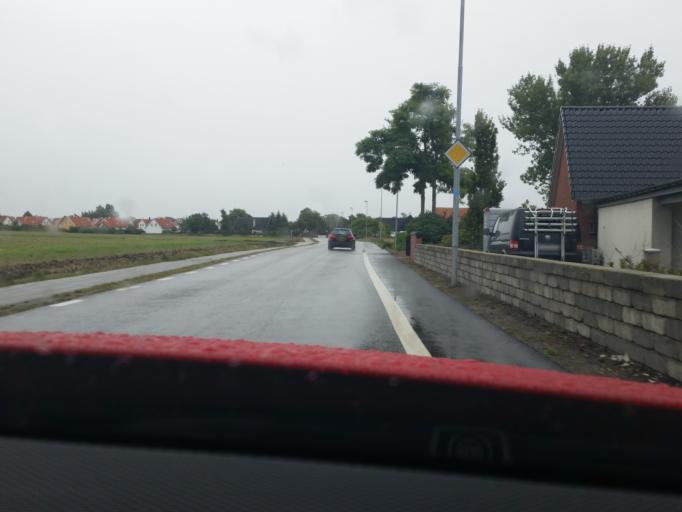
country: SE
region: Skane
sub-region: Malmo
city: Bunkeflostrand
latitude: 55.5337
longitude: 12.9224
